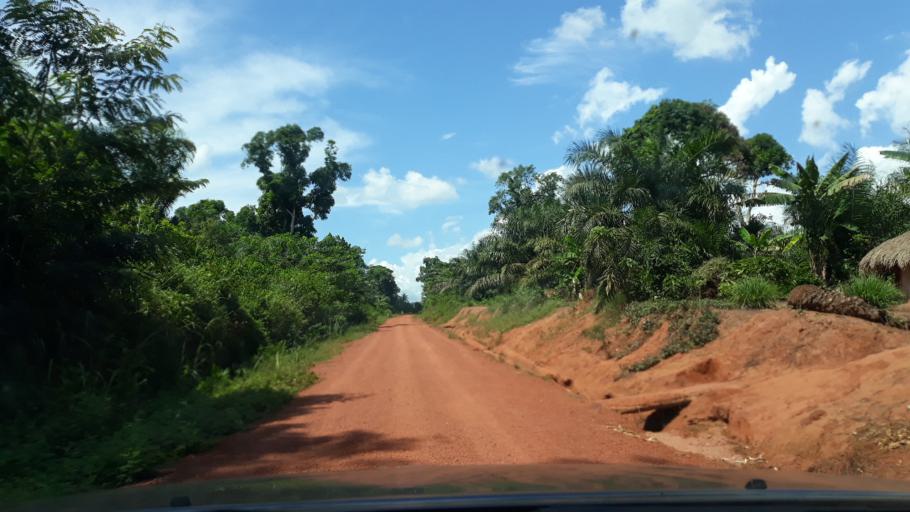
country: CD
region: Equateur
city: Businga
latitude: 3.4074
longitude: 20.3948
